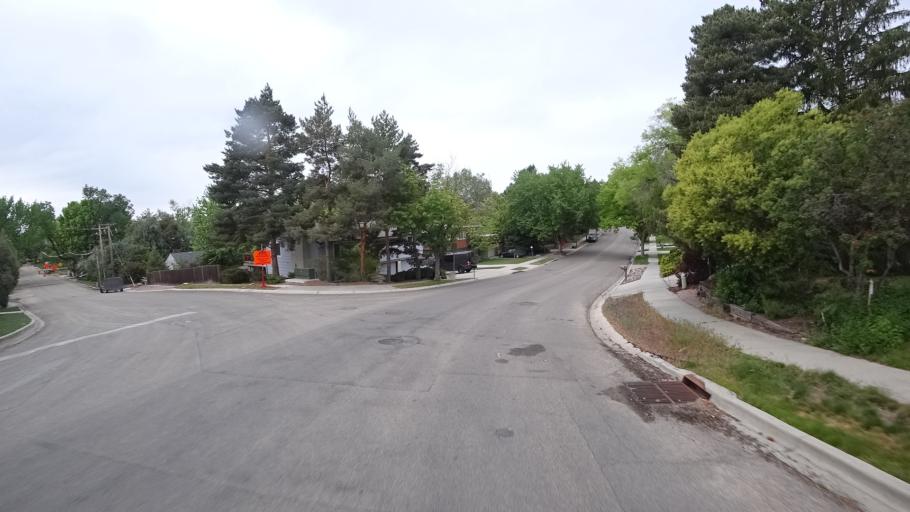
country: US
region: Idaho
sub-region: Ada County
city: Boise
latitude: 43.6120
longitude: -116.1750
